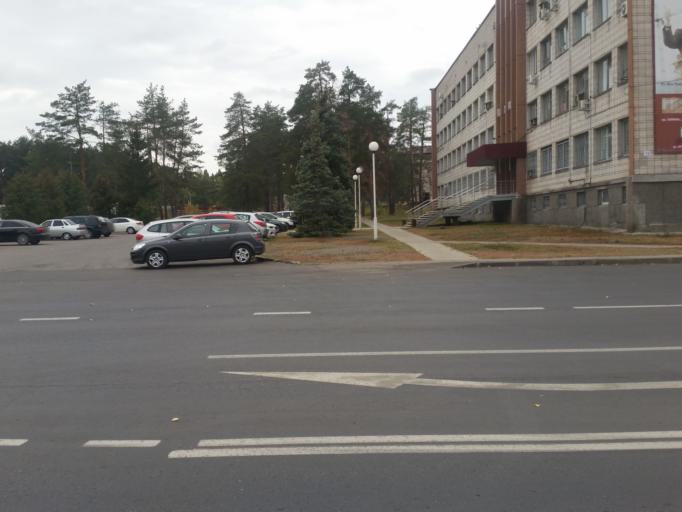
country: RU
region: Ulyanovsk
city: Dimitrovgrad
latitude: 54.2309
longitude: 49.5694
